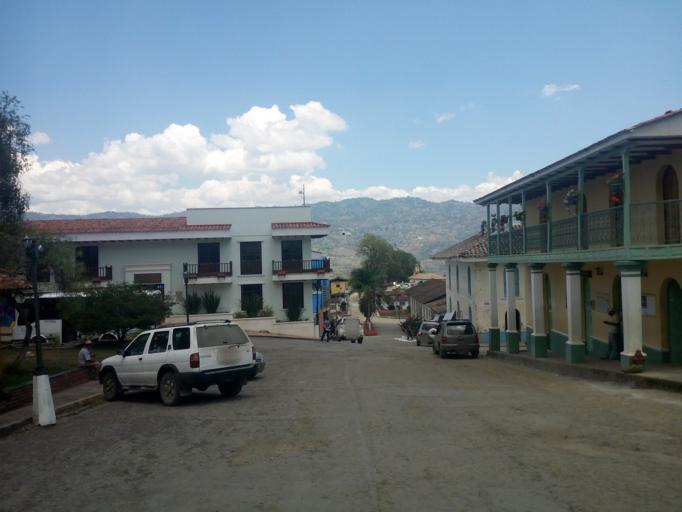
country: CO
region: Boyaca
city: Somondoco
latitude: 4.9859
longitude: -73.4324
